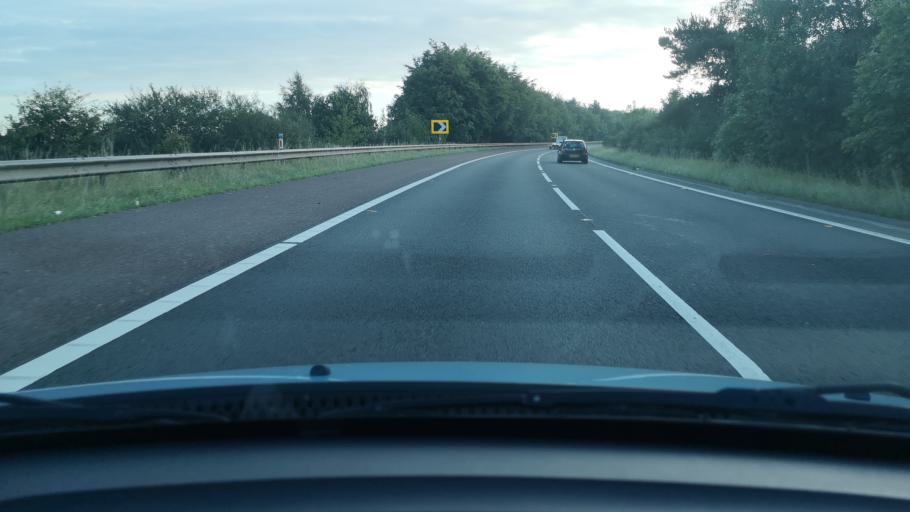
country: GB
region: England
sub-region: East Riding of Yorkshire
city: Rawcliffe
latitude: 53.6831
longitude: -0.9780
